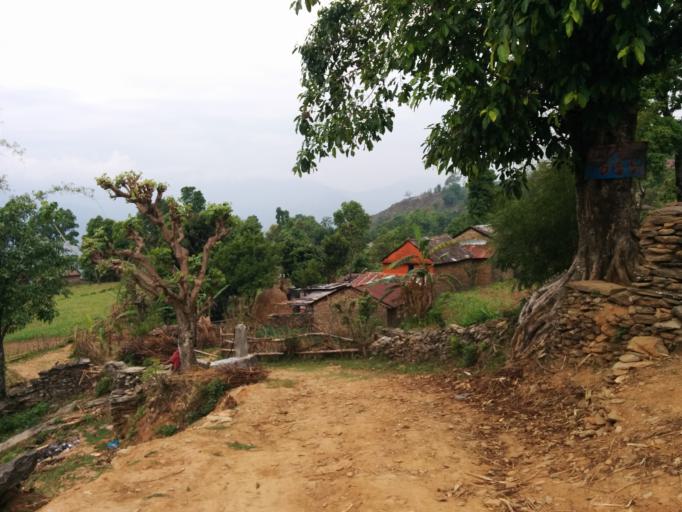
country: NP
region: Western Region
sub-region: Gandaki Zone
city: Pokhara
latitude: 28.2358
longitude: 83.9489
